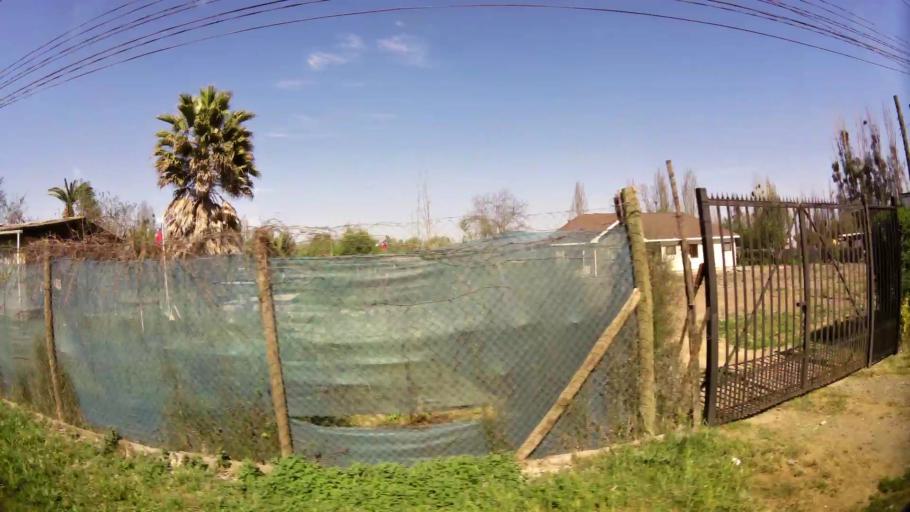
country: CL
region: Santiago Metropolitan
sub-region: Provincia de Talagante
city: Penaflor
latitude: -33.5871
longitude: -70.8760
